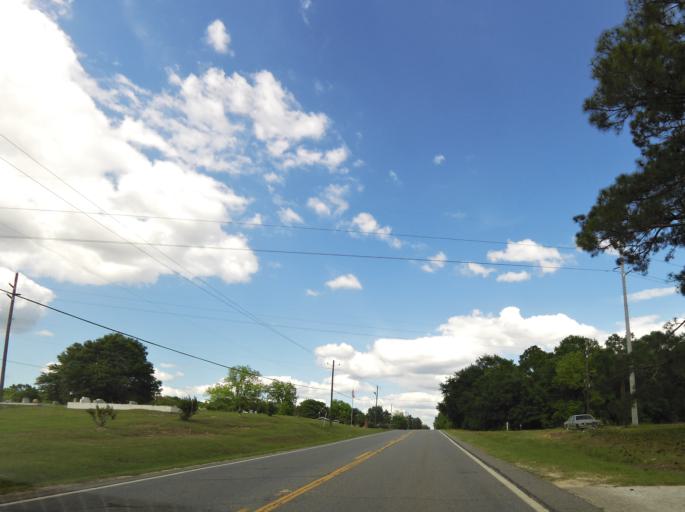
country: US
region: Georgia
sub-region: Treutlen County
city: Soperton
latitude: 32.3725
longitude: -82.6036
